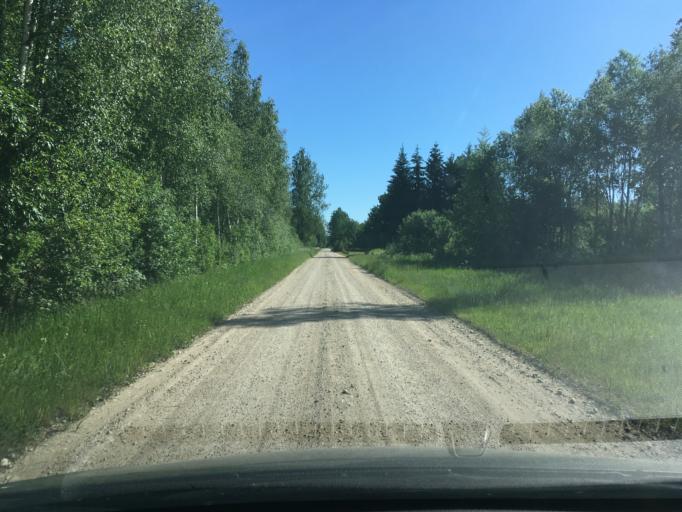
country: EE
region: Laeaene
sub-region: Lihula vald
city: Lihula
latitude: 58.6451
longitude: 23.7779
